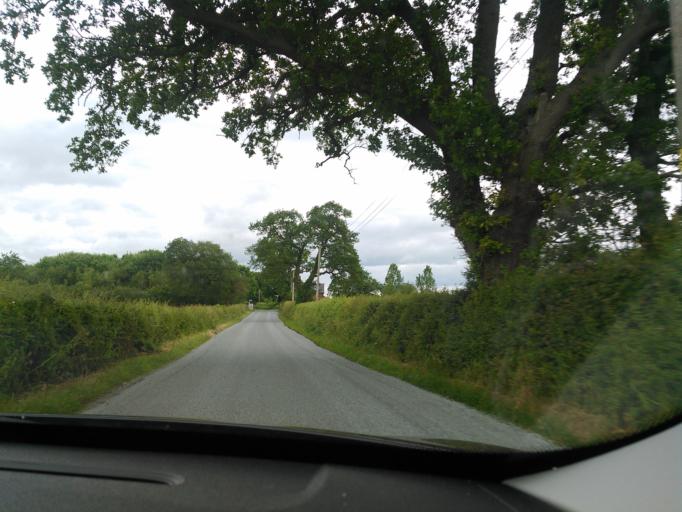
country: GB
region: England
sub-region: Shropshire
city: Wem
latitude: 52.8854
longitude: -2.7502
